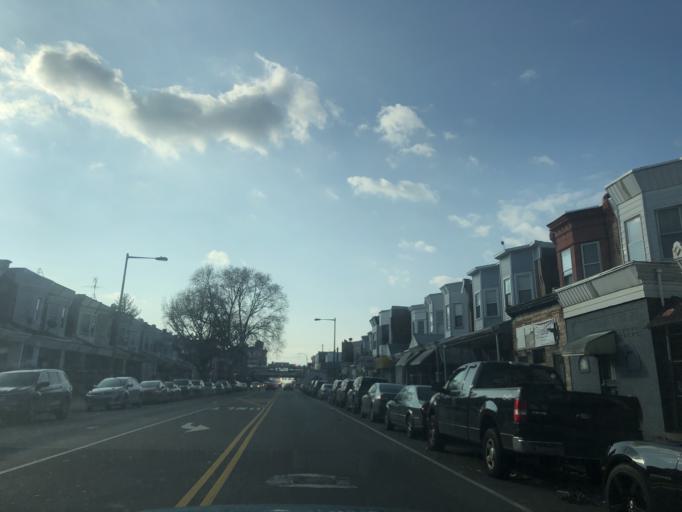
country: US
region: Pennsylvania
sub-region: Delaware County
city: Millbourne
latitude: 39.9630
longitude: -75.2243
